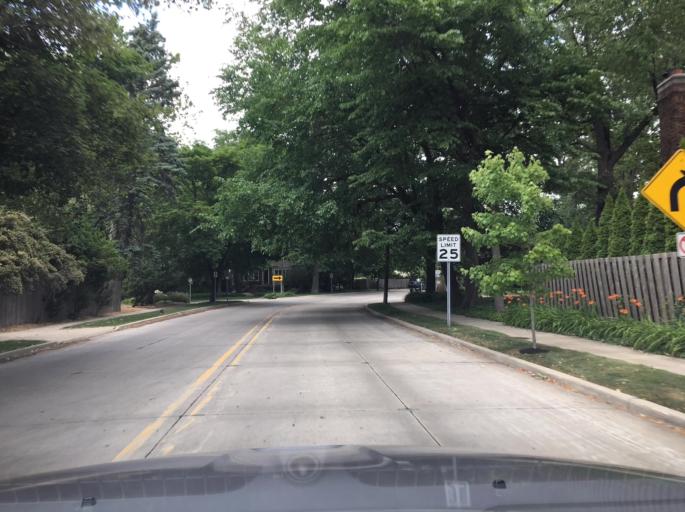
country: US
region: Michigan
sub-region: Oakland County
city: Royal Oak
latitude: 42.4867
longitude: -83.1551
